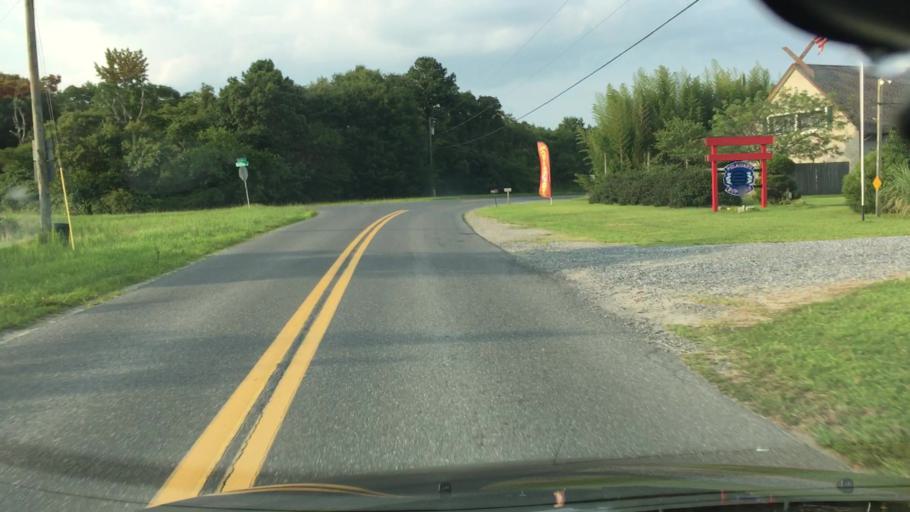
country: US
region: Delaware
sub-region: Sussex County
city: Selbyville
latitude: 38.4650
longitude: -75.1545
